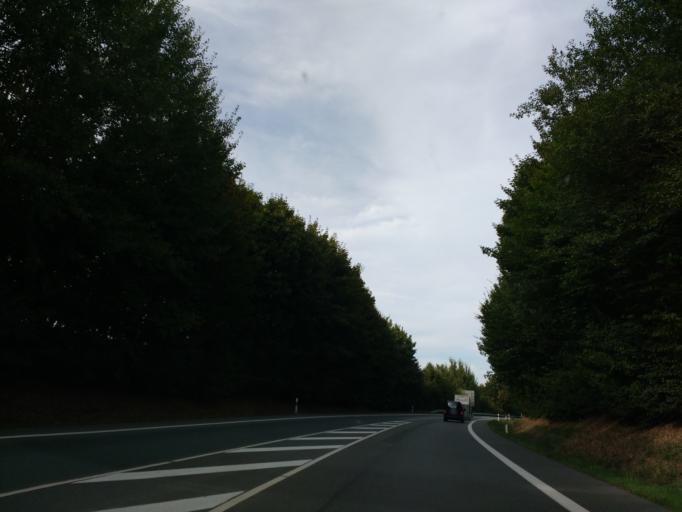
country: DE
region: North Rhine-Westphalia
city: Brakel
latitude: 51.7333
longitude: 9.1661
